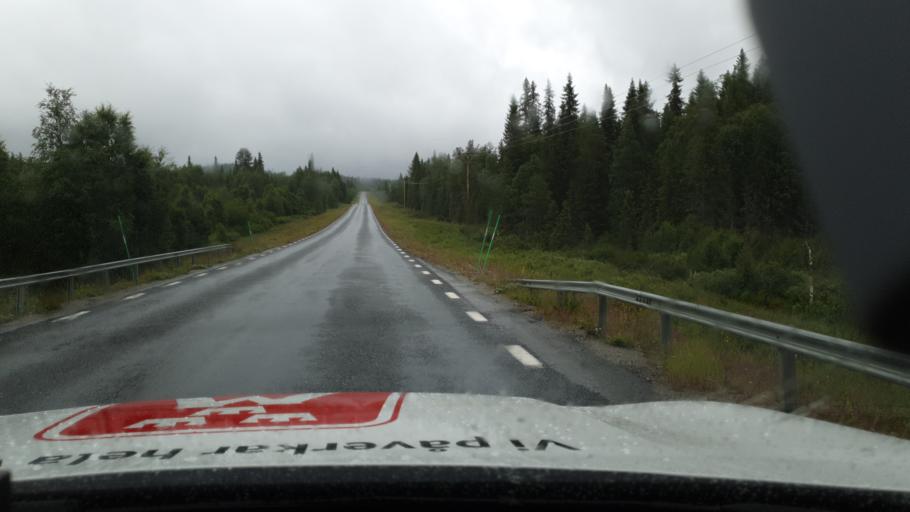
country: SE
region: Vaesterbotten
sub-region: Lycksele Kommun
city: Soderfors
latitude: 64.3730
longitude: 17.9715
